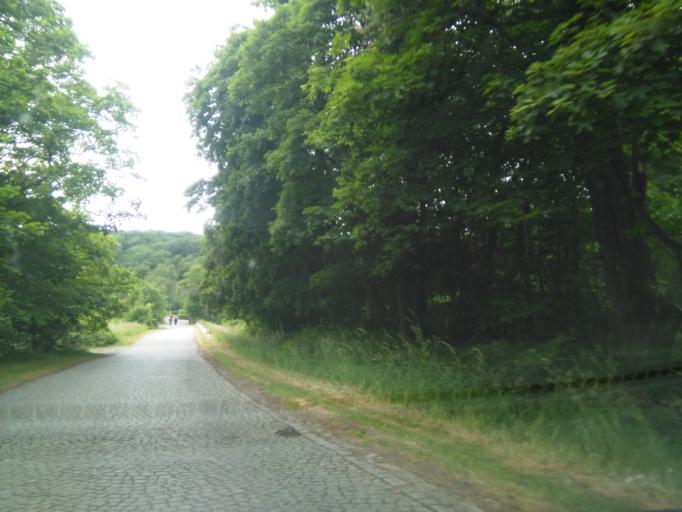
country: DK
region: Capital Region
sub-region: Bornholm Kommune
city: Akirkeby
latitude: 55.1104
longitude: 14.9093
